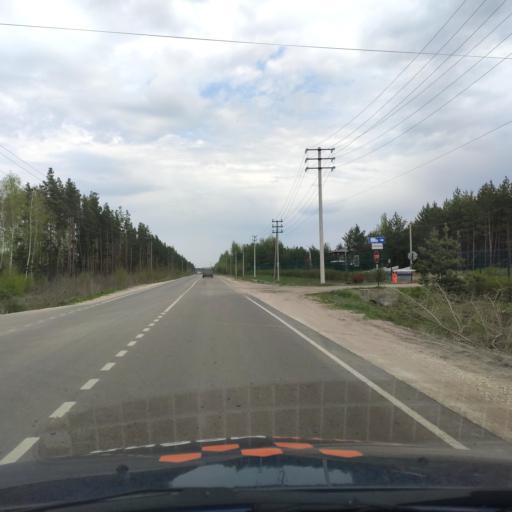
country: RU
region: Voronezj
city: Podgornoye
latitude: 51.8580
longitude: 39.1627
